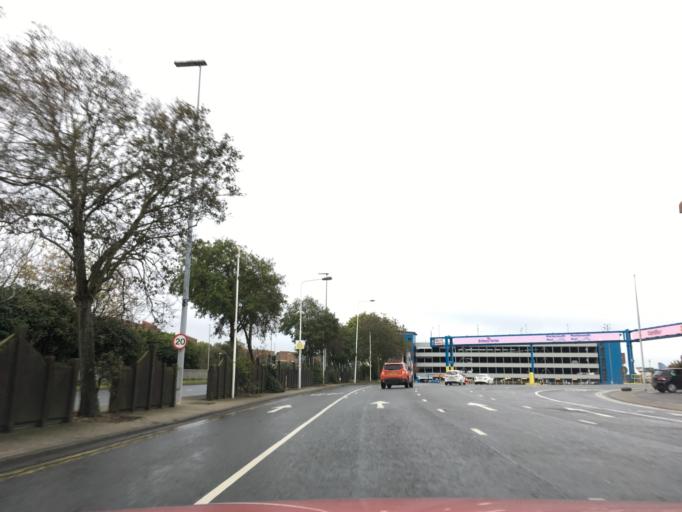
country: GB
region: England
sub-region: Portsmouth
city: Portsmouth
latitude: 50.8121
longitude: -1.0864
